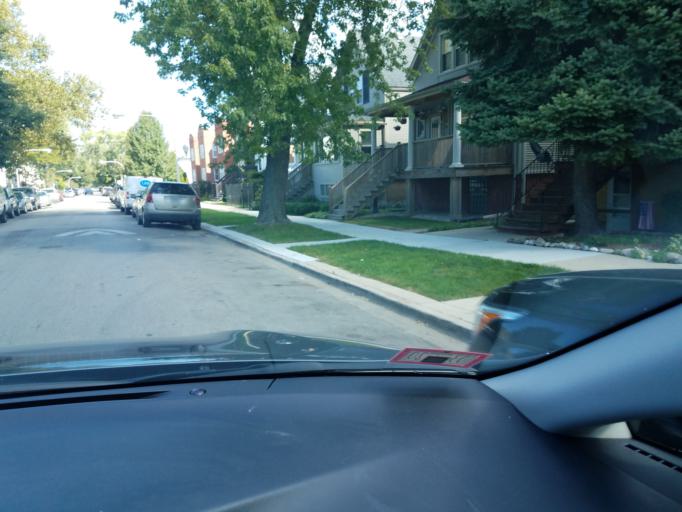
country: US
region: Illinois
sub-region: Cook County
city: Lincolnwood
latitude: 41.9494
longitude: -87.7030
